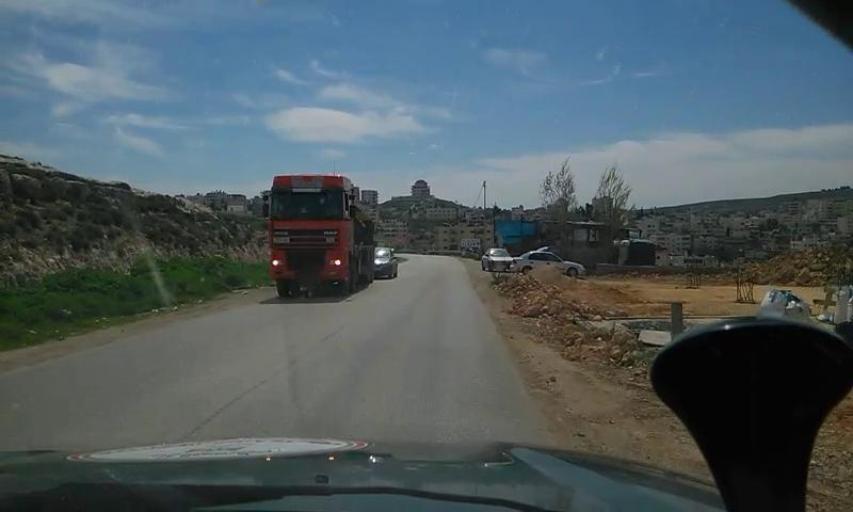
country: PS
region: West Bank
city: Al Judayrah
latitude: 31.8555
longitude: 35.2015
